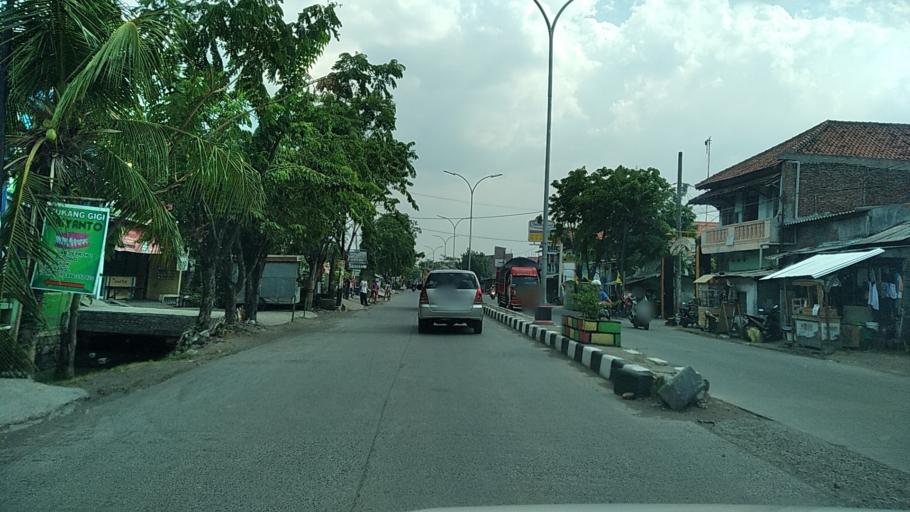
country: ID
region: Central Java
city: Semarang
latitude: -6.9540
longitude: 110.4805
